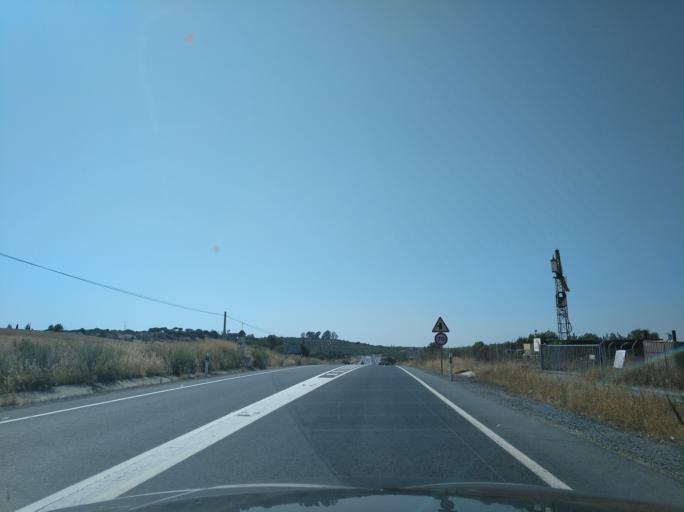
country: ES
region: Andalusia
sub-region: Provincia de Huelva
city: Gibraleon
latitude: 37.3808
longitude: -6.9868
